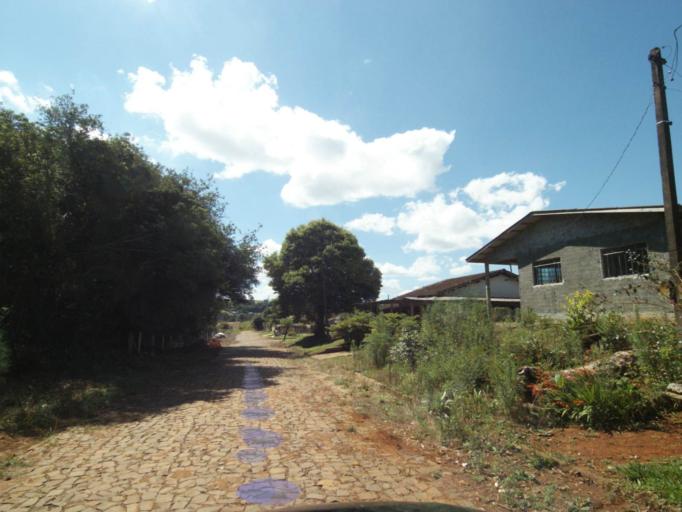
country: BR
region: Parana
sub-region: Coronel Vivida
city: Coronel Vivida
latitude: -26.1488
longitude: -52.3831
